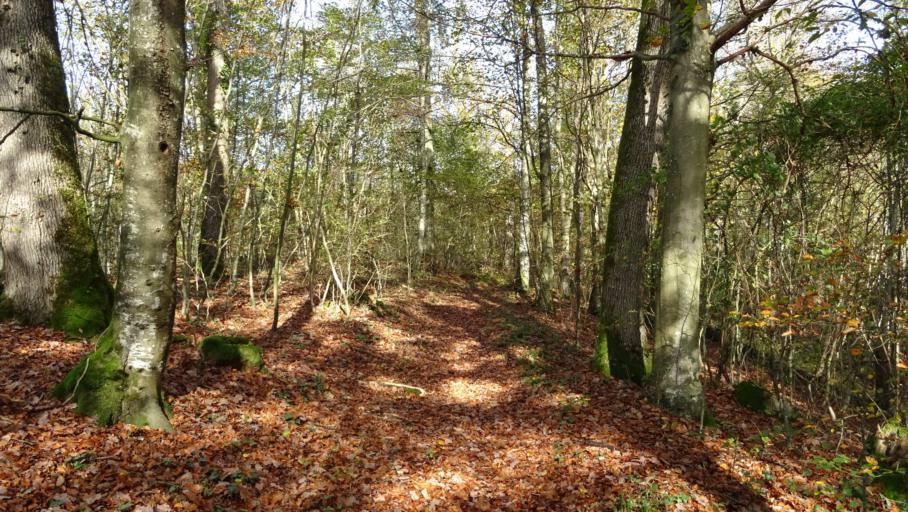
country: DE
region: Baden-Wuerttemberg
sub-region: Karlsruhe Region
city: Binau
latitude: 49.3711
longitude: 9.0465
